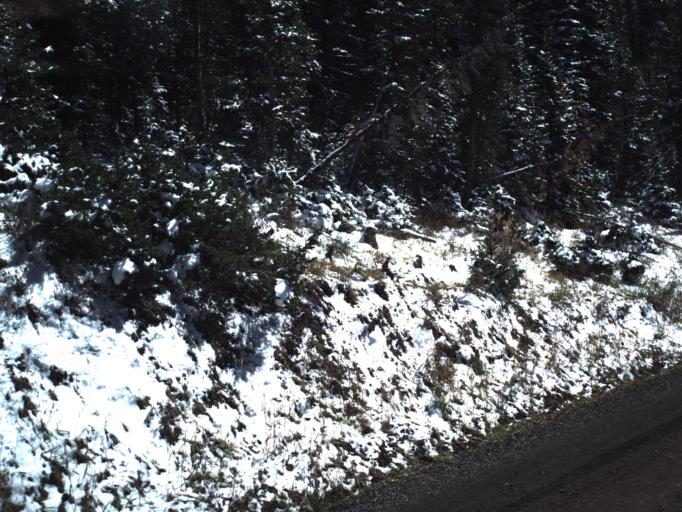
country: US
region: Utah
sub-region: Piute County
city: Junction
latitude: 38.3038
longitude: -112.3617
